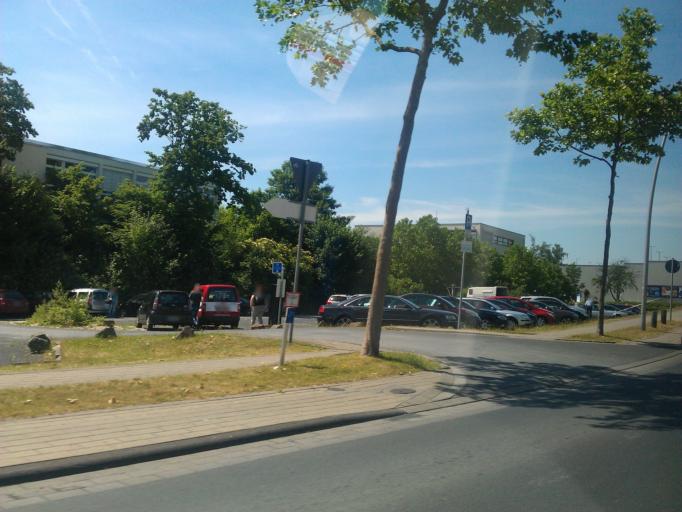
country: DE
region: North Rhine-Westphalia
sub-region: Regierungsbezirk Koln
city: Siegburg
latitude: 50.7924
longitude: 7.2042
